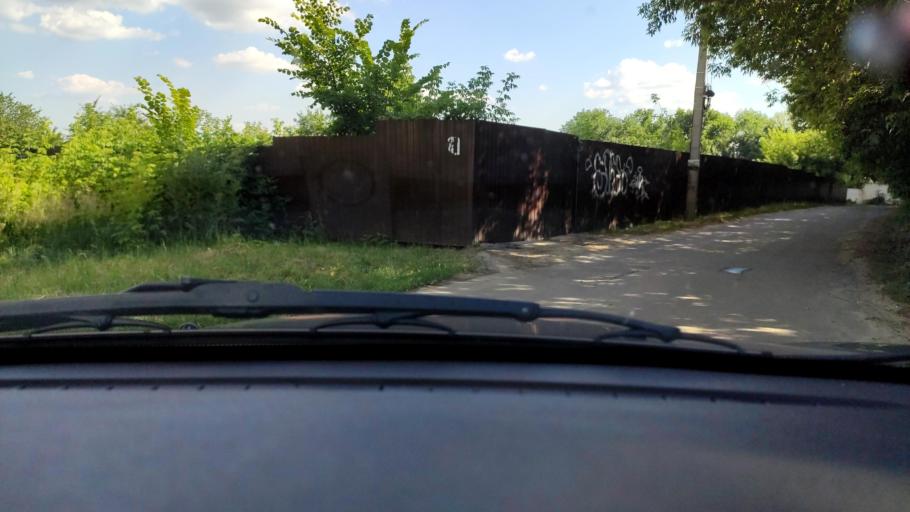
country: RU
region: Voronezj
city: Ramon'
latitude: 51.8249
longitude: 39.2706
